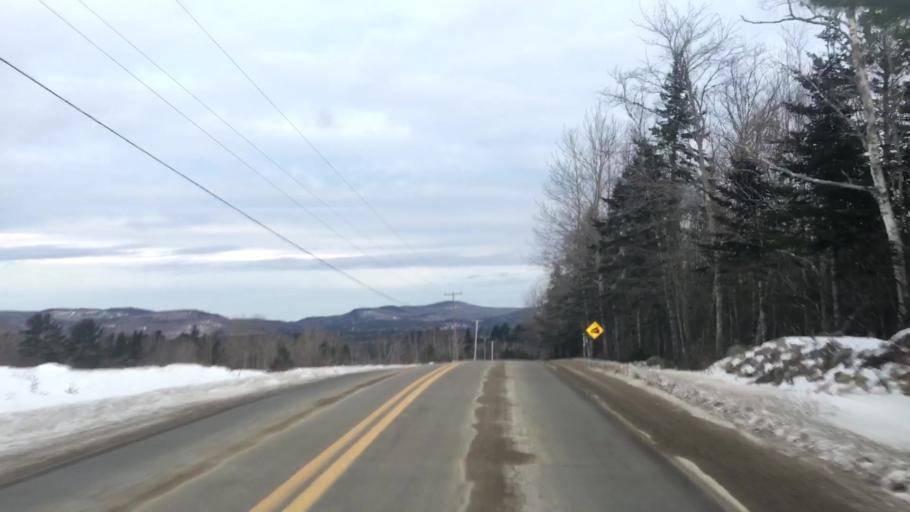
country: US
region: Maine
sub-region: Hancock County
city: Franklin
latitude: 44.8451
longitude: -68.3277
